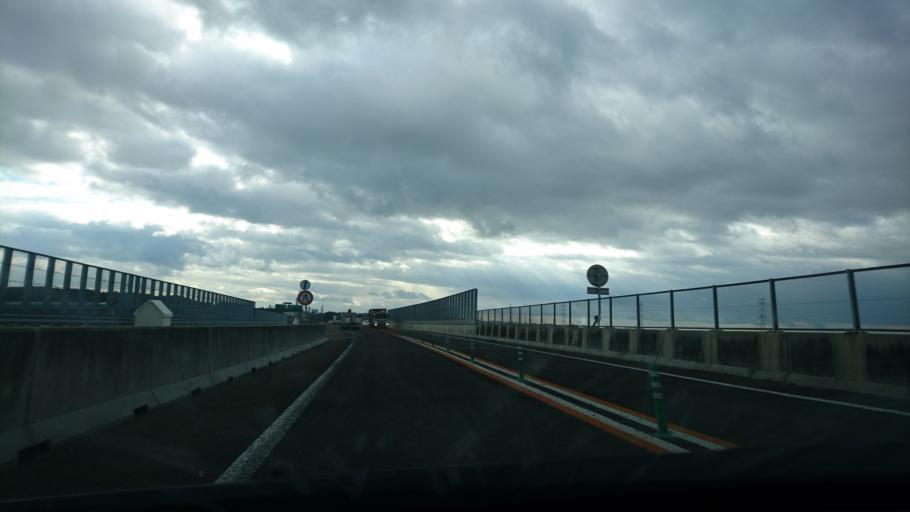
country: JP
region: Miyagi
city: Rifu
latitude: 38.3161
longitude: 140.9700
